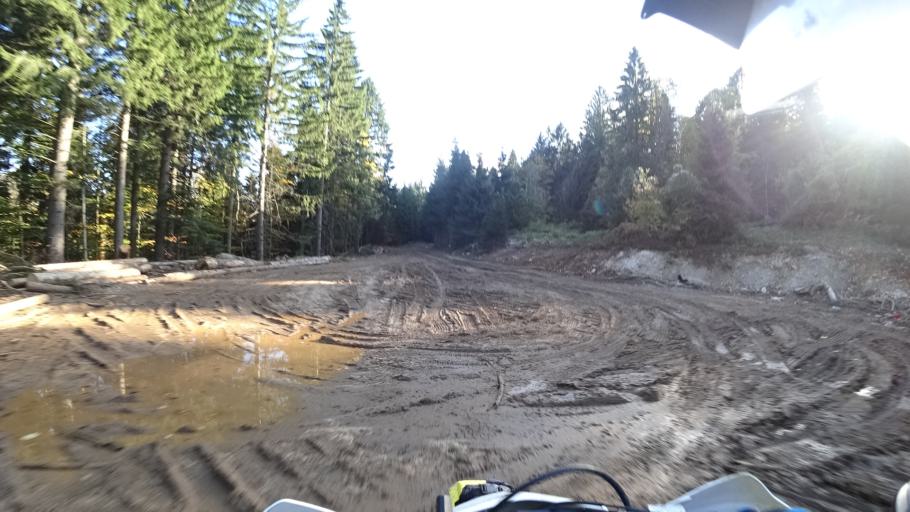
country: HR
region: Karlovacka
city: Plaski
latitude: 44.9526
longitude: 15.4494
